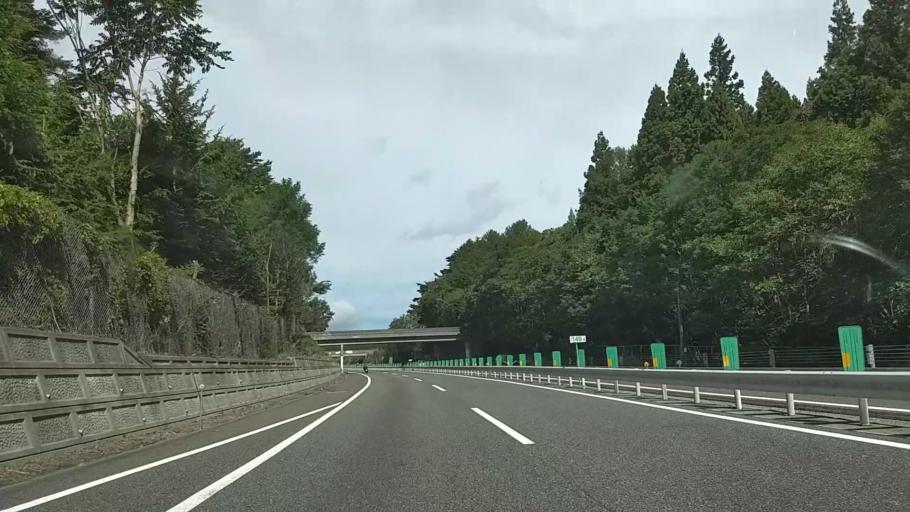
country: JP
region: Nagano
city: Chino
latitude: 35.8773
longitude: 138.3044
